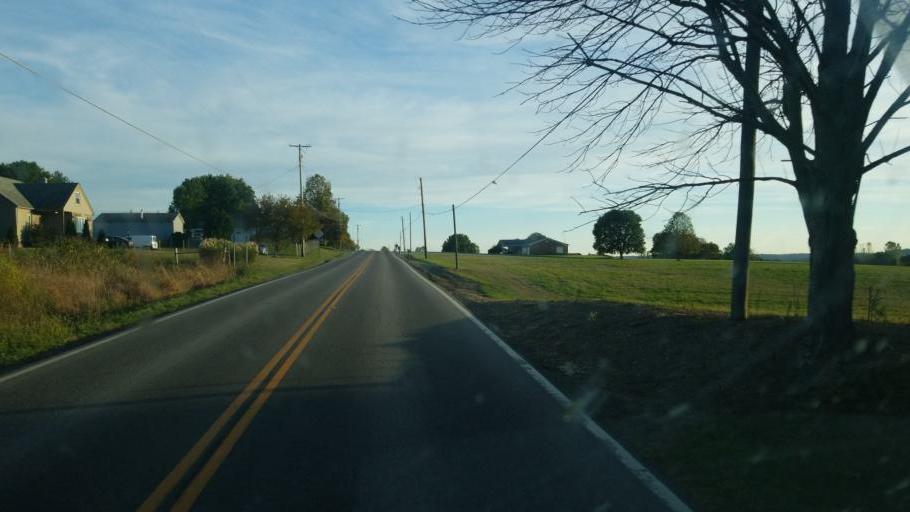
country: US
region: Ohio
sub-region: Ashland County
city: Ashland
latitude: 40.8636
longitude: -82.4030
